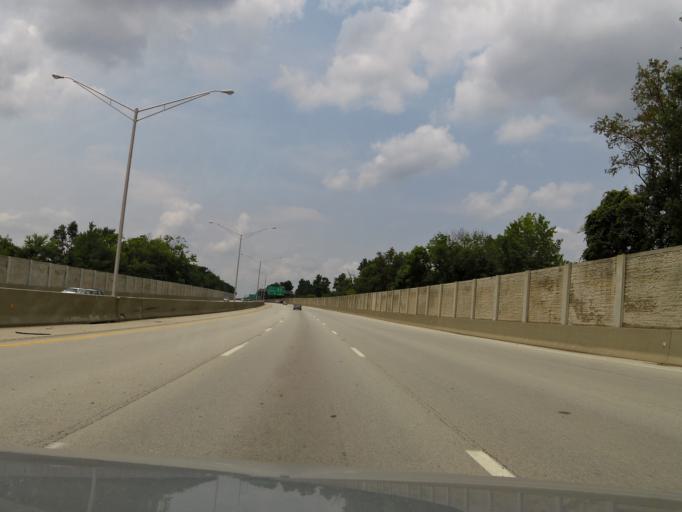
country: US
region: Kentucky
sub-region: Jefferson County
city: Graymoor-Devondale
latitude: 38.2696
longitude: -85.6265
